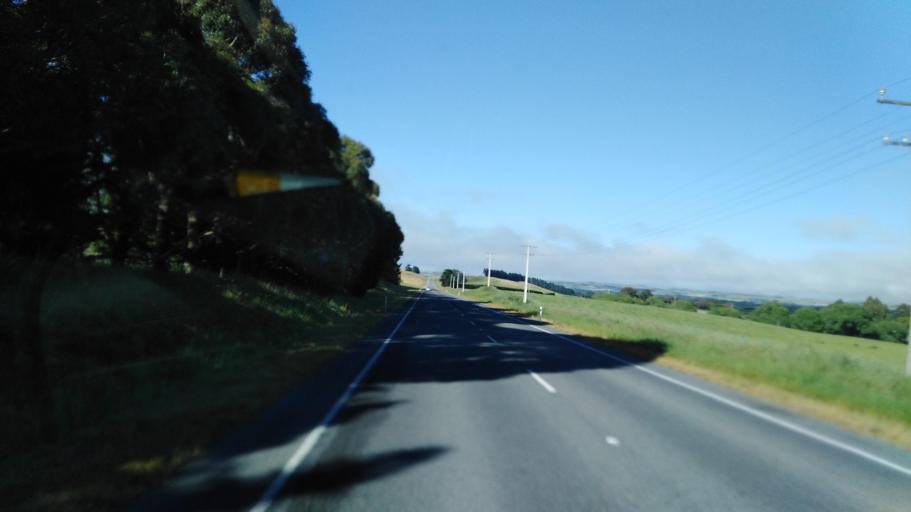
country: NZ
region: Canterbury
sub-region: Hurunui District
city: Amberley
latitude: -42.9284
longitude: 172.7192
